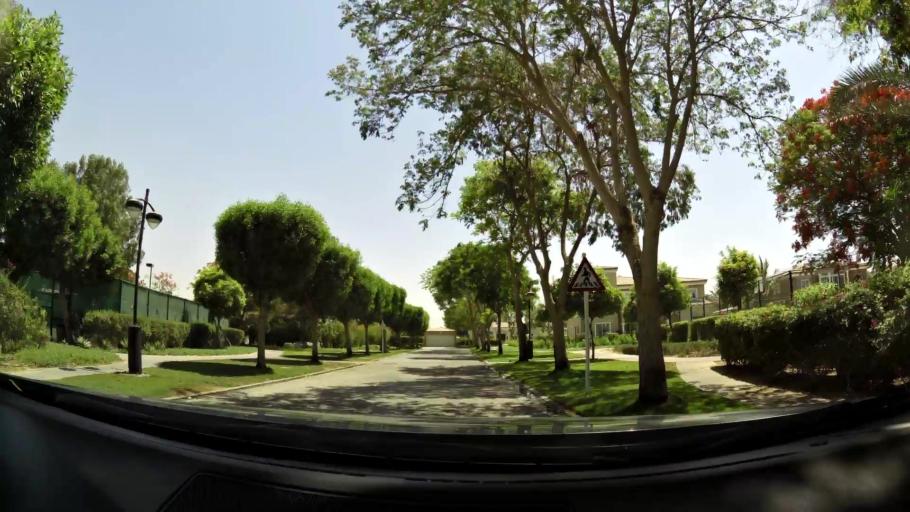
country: AE
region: Dubai
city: Dubai
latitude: 24.9983
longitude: 55.1585
